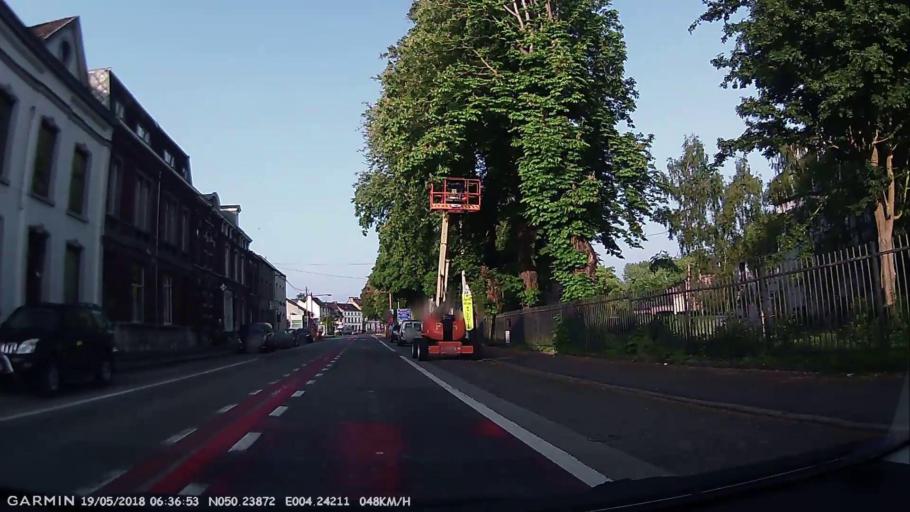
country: BE
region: Wallonia
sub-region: Province du Hainaut
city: Beaumont
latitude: 50.2387
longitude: 4.2420
